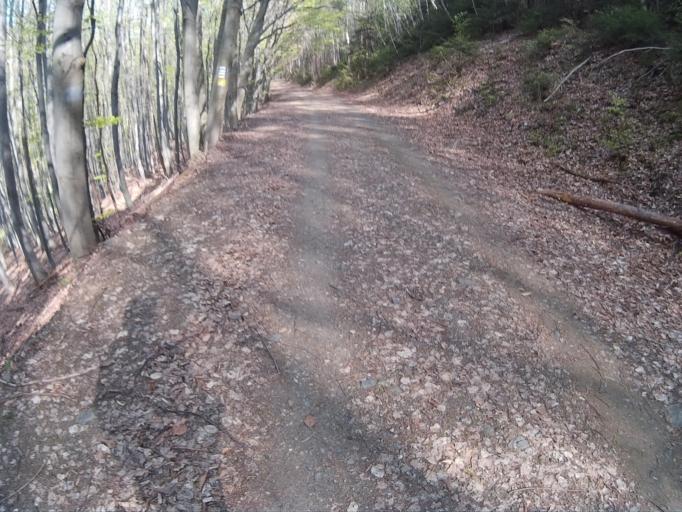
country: AT
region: Burgenland
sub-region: Politischer Bezirk Oberwart
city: Rechnitz
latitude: 47.3394
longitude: 16.4540
